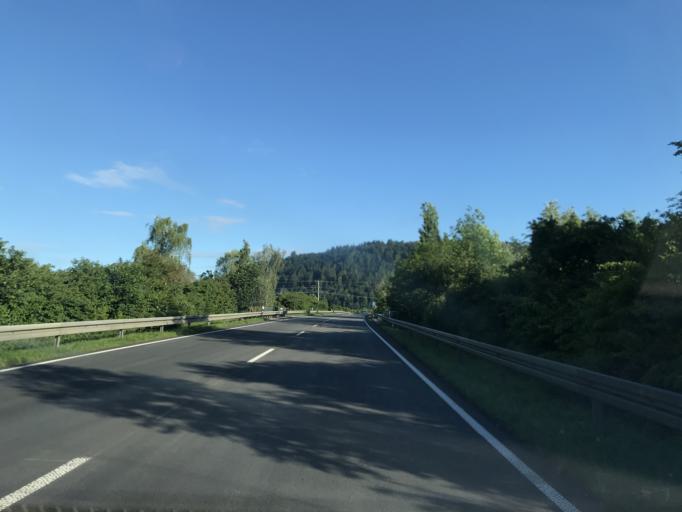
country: DE
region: Baden-Wuerttemberg
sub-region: Freiburg Region
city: Maulburg
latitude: 47.6439
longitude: 7.7981
